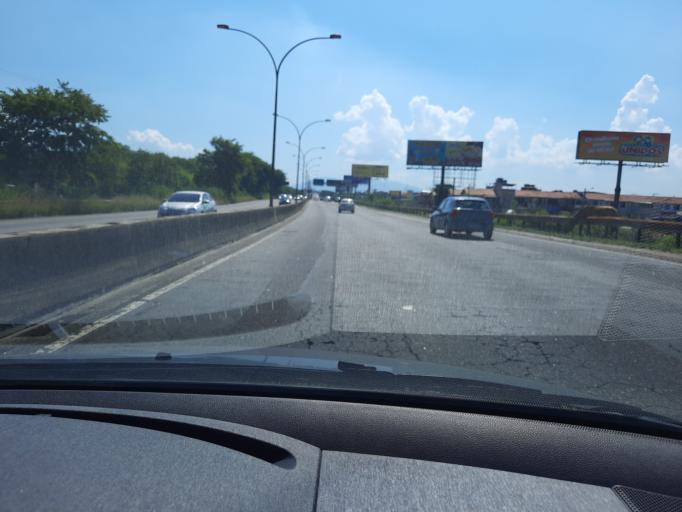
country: BR
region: Rio de Janeiro
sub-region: Duque De Caxias
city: Duque de Caxias
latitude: -22.8081
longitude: -43.2774
